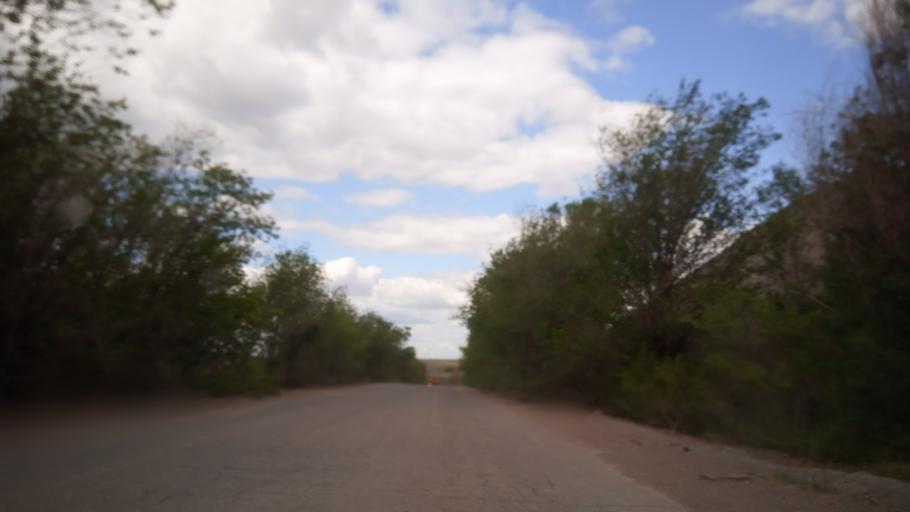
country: RU
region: Orenburg
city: Novotroitsk
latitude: 51.2500
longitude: 58.3641
